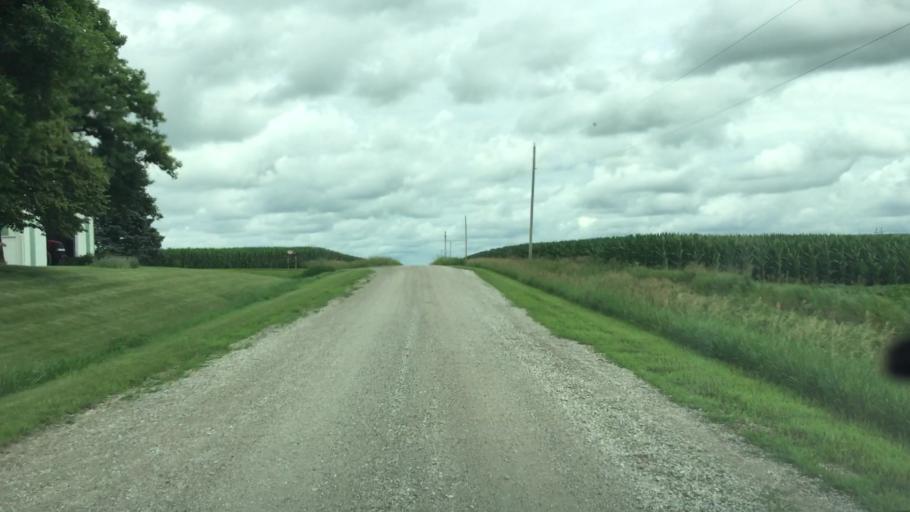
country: US
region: Iowa
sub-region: Jasper County
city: Monroe
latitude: 41.5695
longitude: -93.1208
